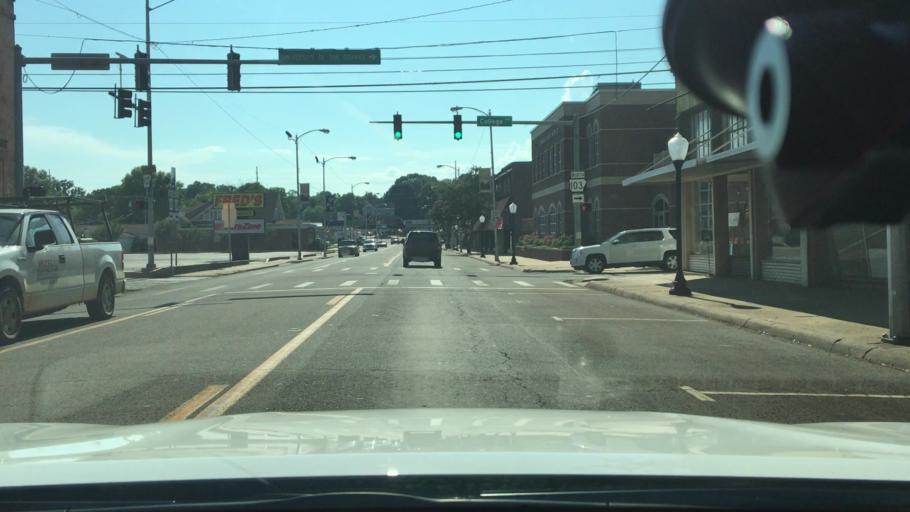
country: US
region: Arkansas
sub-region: Johnson County
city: Clarksville
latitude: 35.4712
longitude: -93.4661
